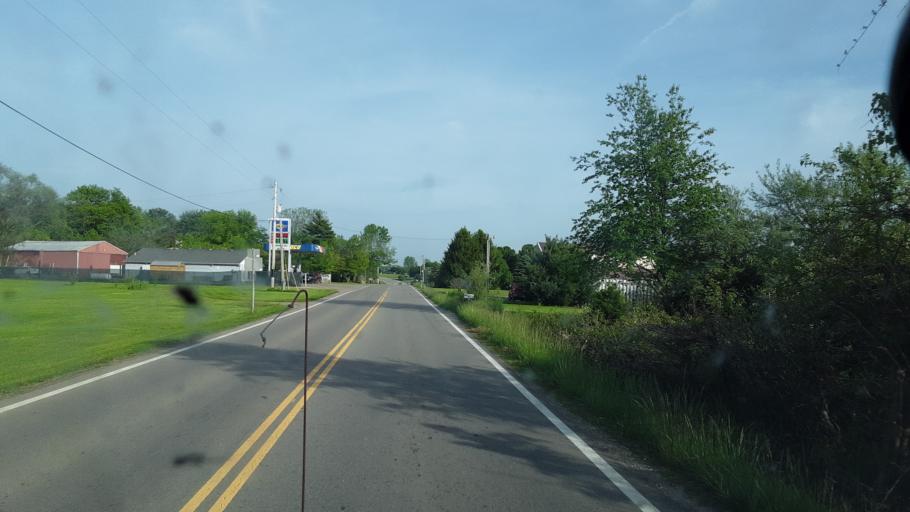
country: US
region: Ohio
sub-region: Ross County
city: Kingston
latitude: 39.5314
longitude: -82.8403
